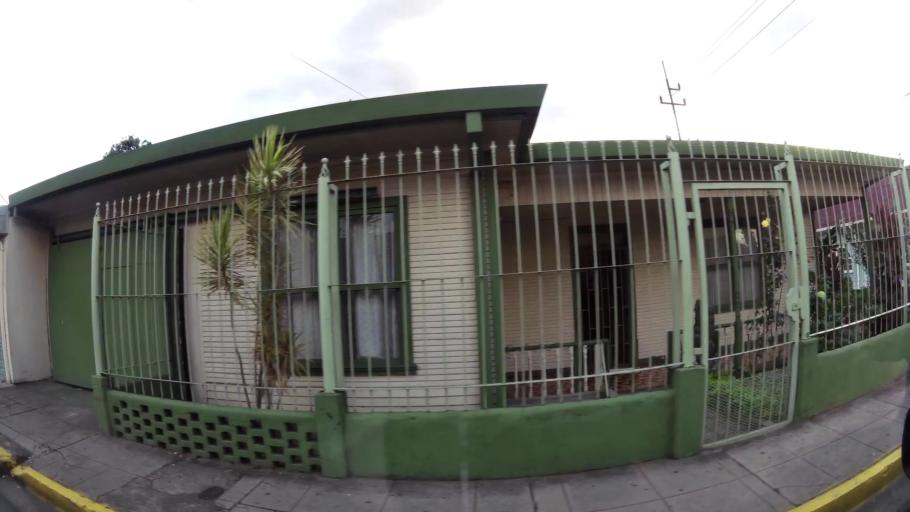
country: CR
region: Heredia
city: Heredia
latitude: 9.9976
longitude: -84.1217
